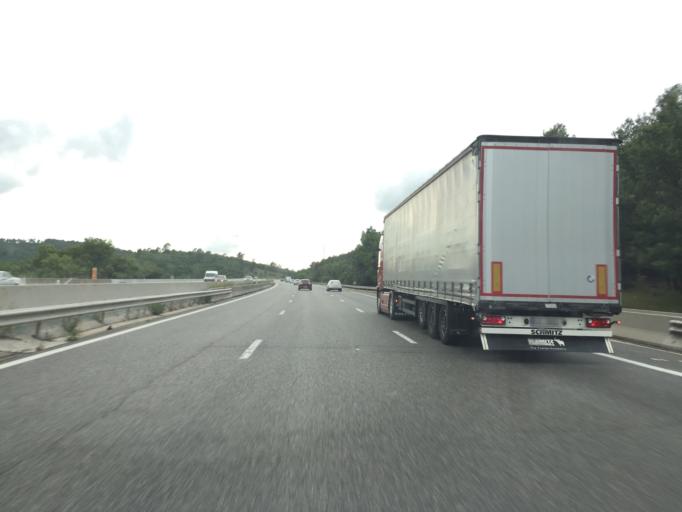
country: FR
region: Provence-Alpes-Cote d'Azur
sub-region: Departement du Var
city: Besse-sur-Issole
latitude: 43.4107
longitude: 6.1532
